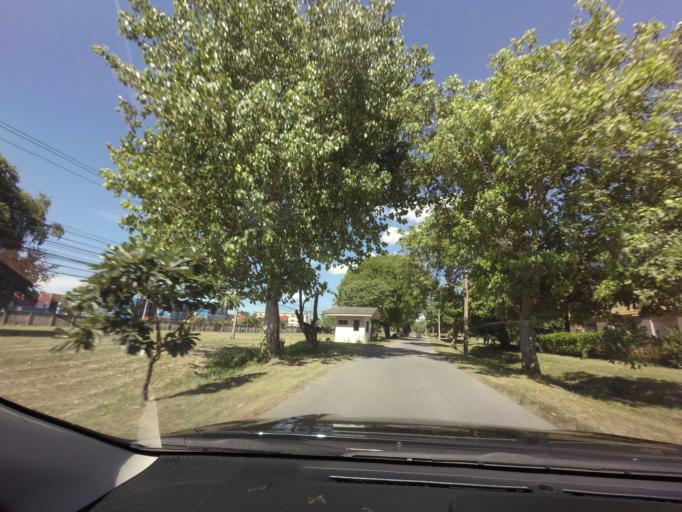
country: TH
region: Chon Buri
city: Bang Lamung
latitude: 13.1058
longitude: 100.9246
